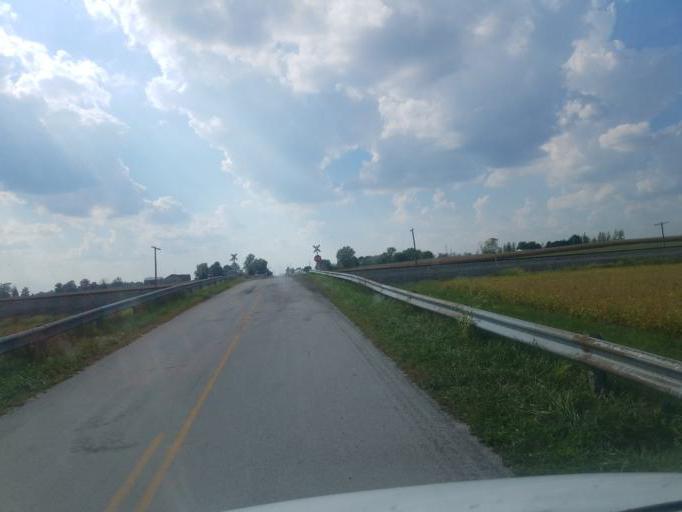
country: US
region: Ohio
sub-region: Hardin County
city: Kenton
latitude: 40.7465
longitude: -83.6423
